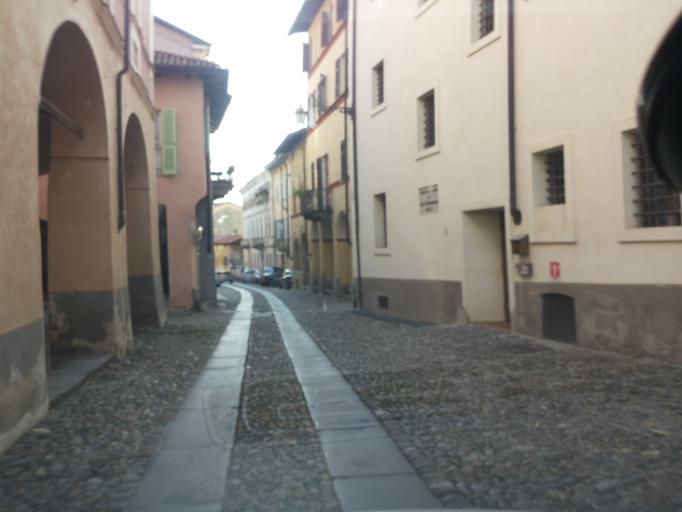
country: IT
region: Piedmont
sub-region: Provincia di Biella
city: Biella
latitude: 45.5657
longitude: 8.0451
